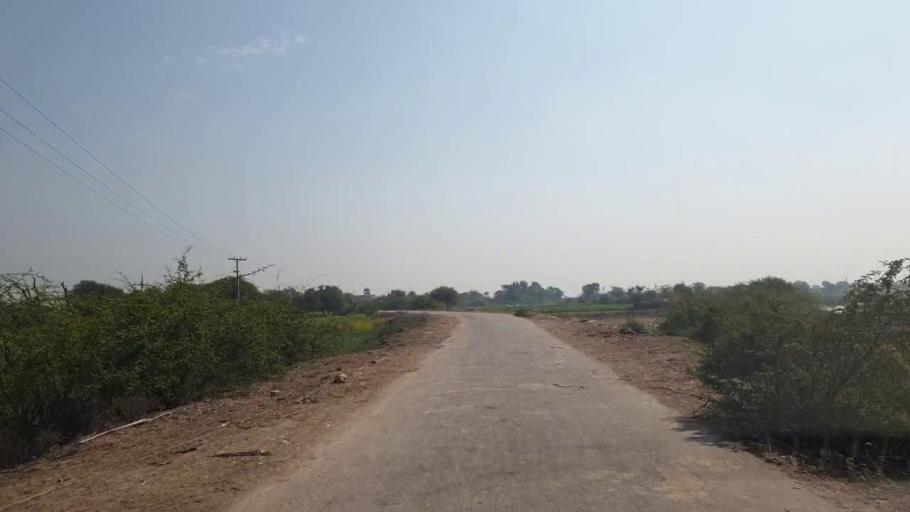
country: PK
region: Sindh
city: Chambar
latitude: 25.3395
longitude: 68.8514
